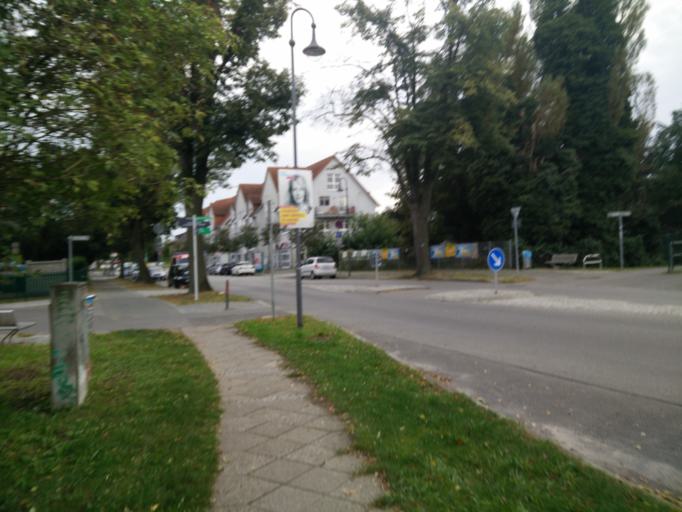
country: DE
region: Brandenburg
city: Falkensee
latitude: 52.5623
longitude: 13.0875
